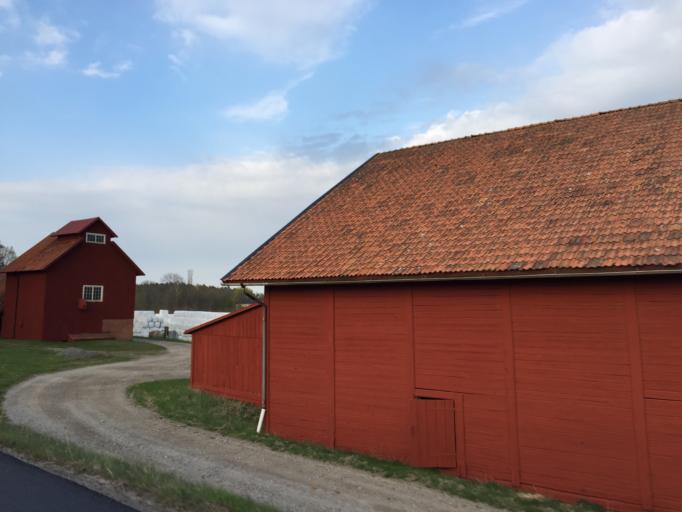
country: SE
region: Soedermanland
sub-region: Trosa Kommun
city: Vagnharad
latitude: 59.0344
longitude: 17.5985
